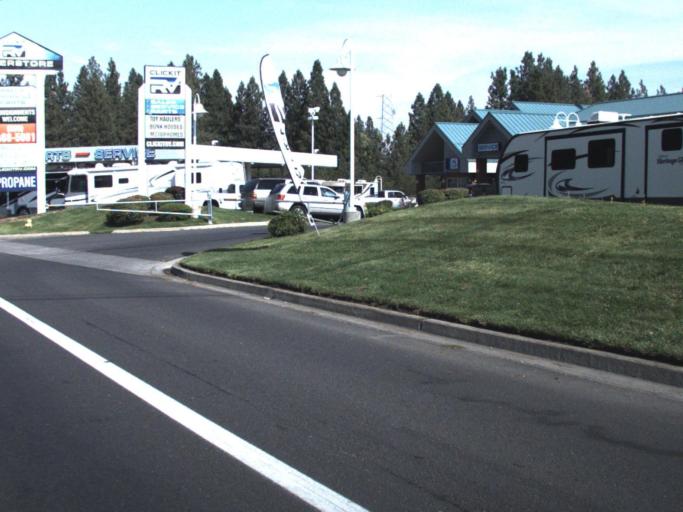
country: US
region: Washington
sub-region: Spokane County
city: Country Homes
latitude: 47.7542
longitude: -117.3974
